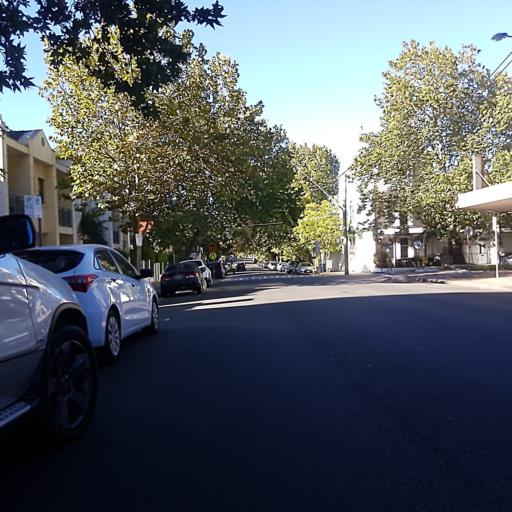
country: AU
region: New South Wales
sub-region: North Sydney
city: North Sydney
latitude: -33.8328
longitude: 151.2054
